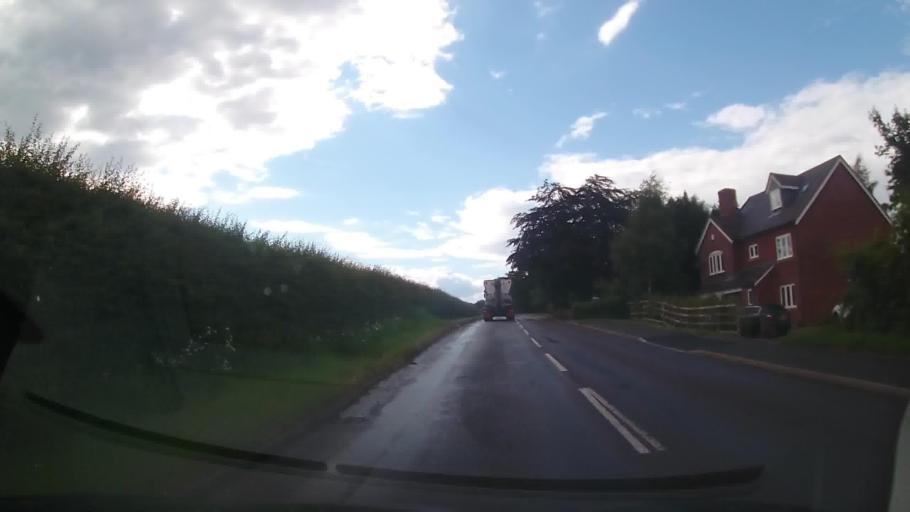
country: GB
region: England
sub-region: Telford and Wrekin
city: Ironbridge
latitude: 52.6605
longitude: -2.4909
